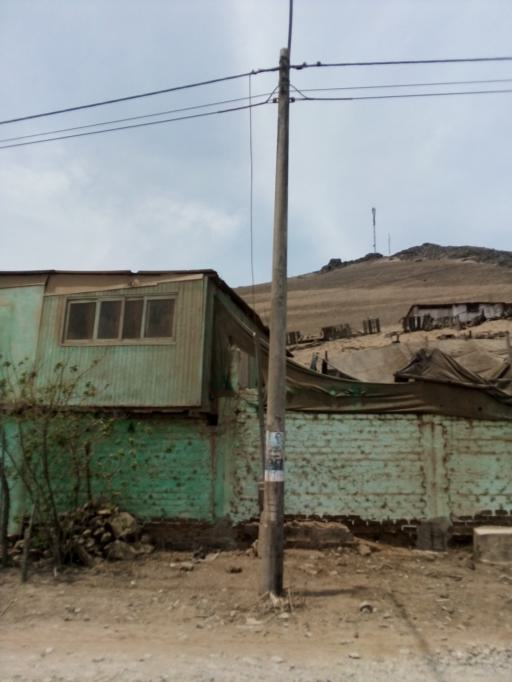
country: PE
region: Lima
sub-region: Lima
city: Santa Rosa
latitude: -11.8209
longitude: -77.1601
